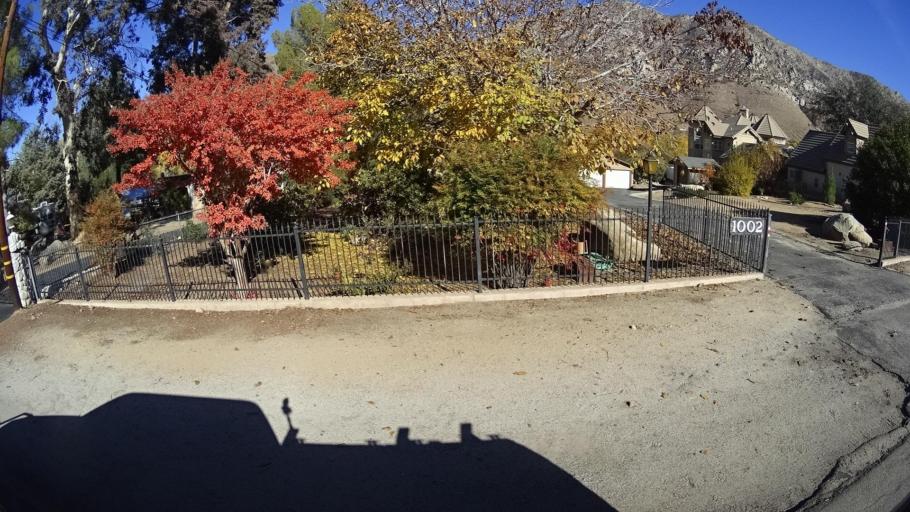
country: US
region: California
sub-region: Kern County
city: Kernville
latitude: 35.7684
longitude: -118.4346
